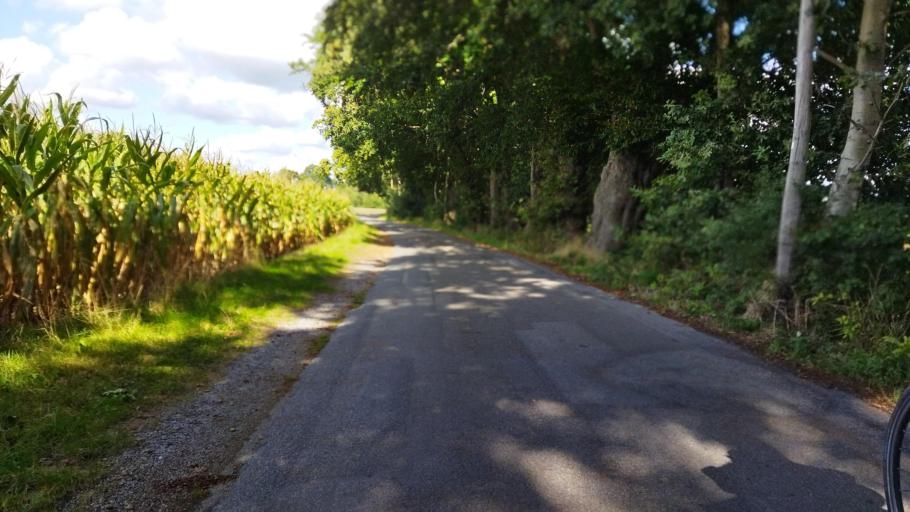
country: DE
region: Lower Saxony
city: Emsburen
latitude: 52.3979
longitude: 7.3232
